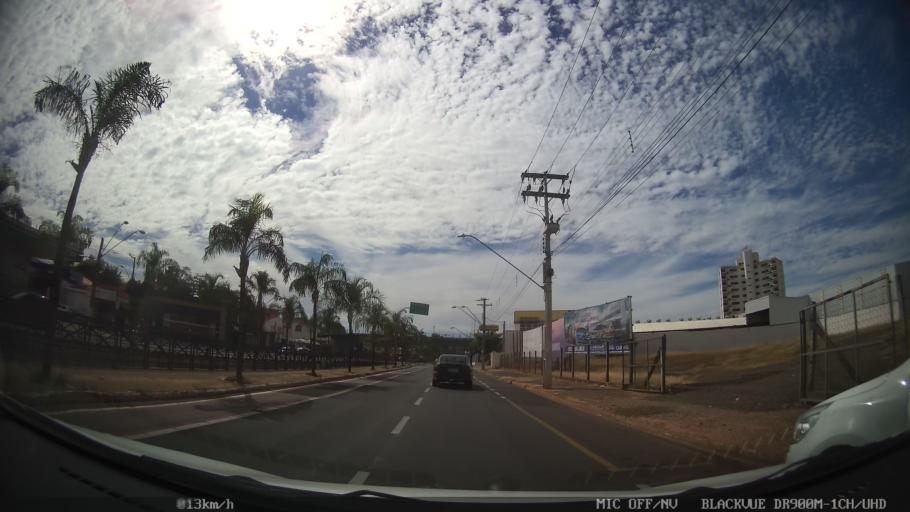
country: BR
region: Sao Paulo
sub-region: Catanduva
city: Catanduva
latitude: -21.1419
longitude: -48.9694
